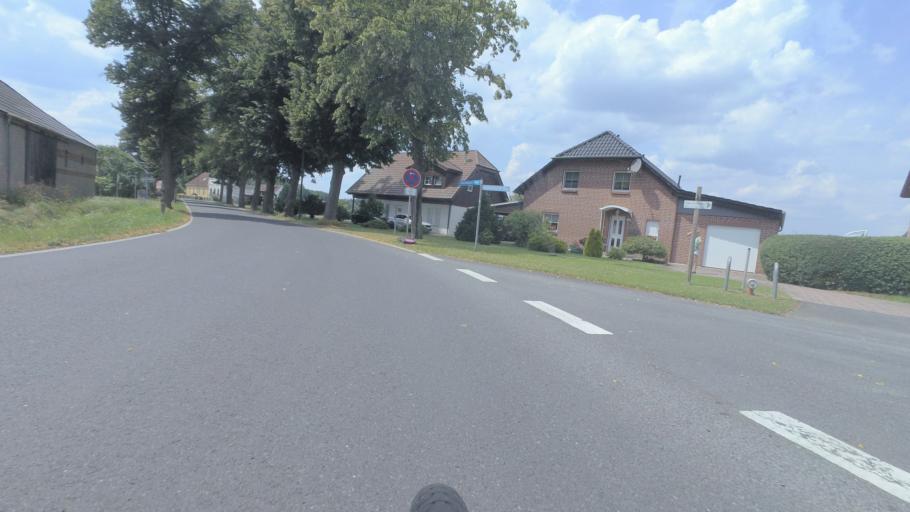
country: DE
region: Brandenburg
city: Luckenwalde
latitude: 52.1200
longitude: 13.2454
